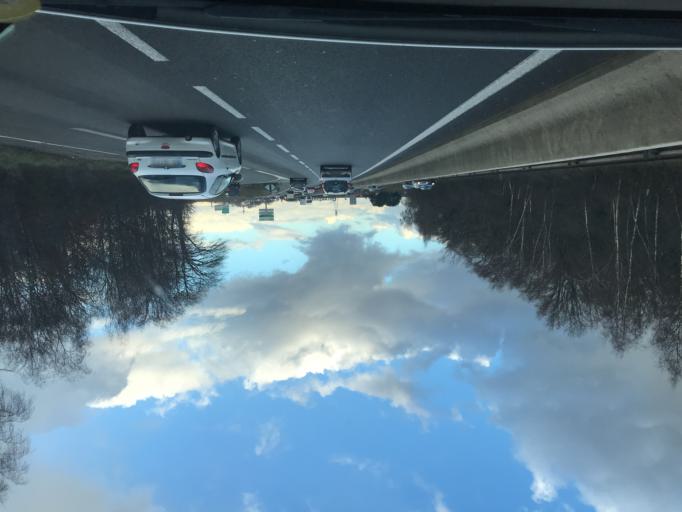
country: FR
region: Ile-de-France
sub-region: Departement de Seine-et-Marne
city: Lesigny
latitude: 48.7703
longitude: 2.6124
